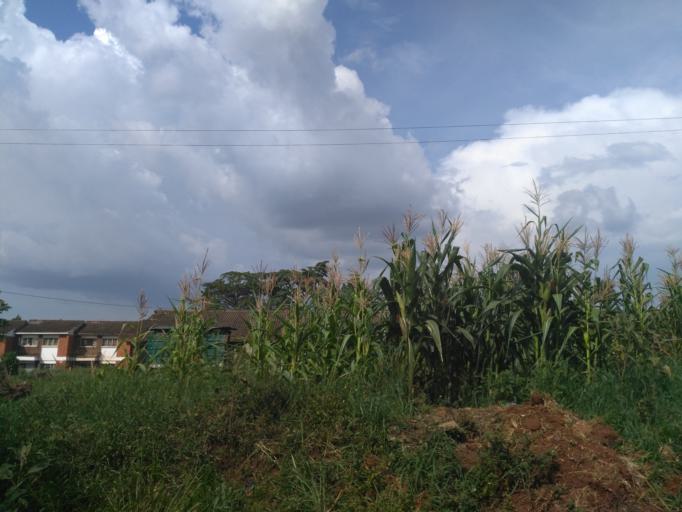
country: UG
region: Eastern Region
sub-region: Jinja District
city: Jinja
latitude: 0.4397
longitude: 33.2071
